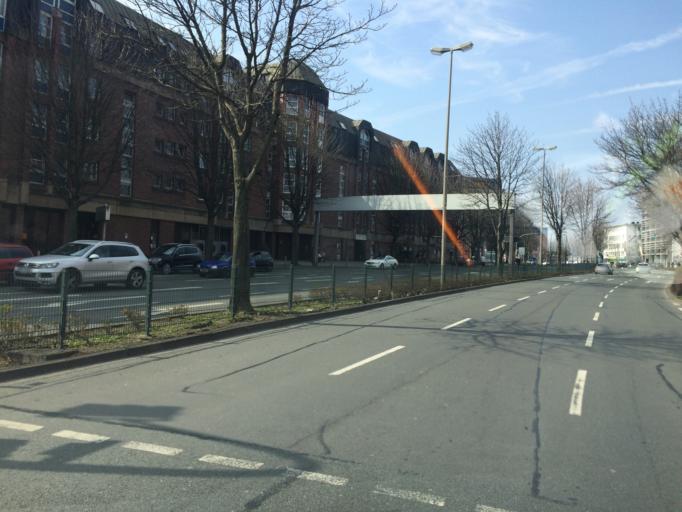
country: DE
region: North Rhine-Westphalia
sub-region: Regierungsbezirk Arnsberg
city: Dortmund
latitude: 51.5172
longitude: 7.4689
